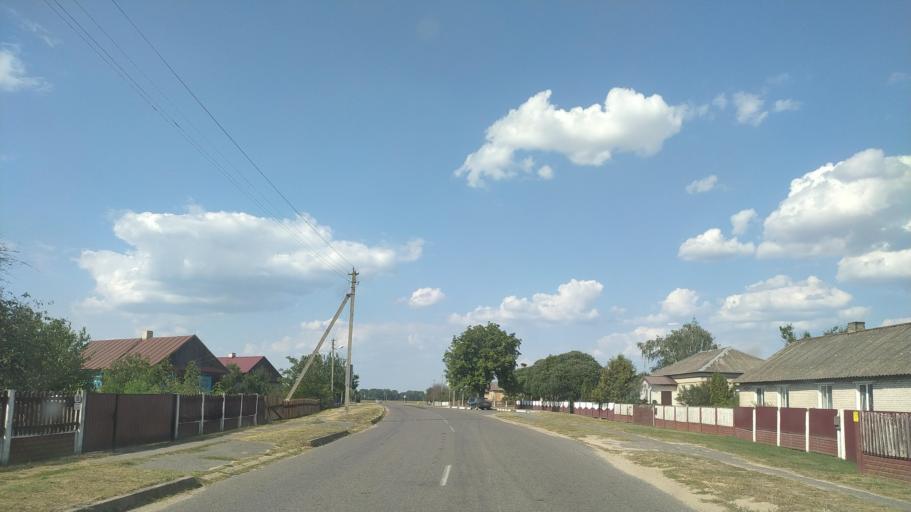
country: BY
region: Brest
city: Drahichyn
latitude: 52.1200
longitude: 25.1170
